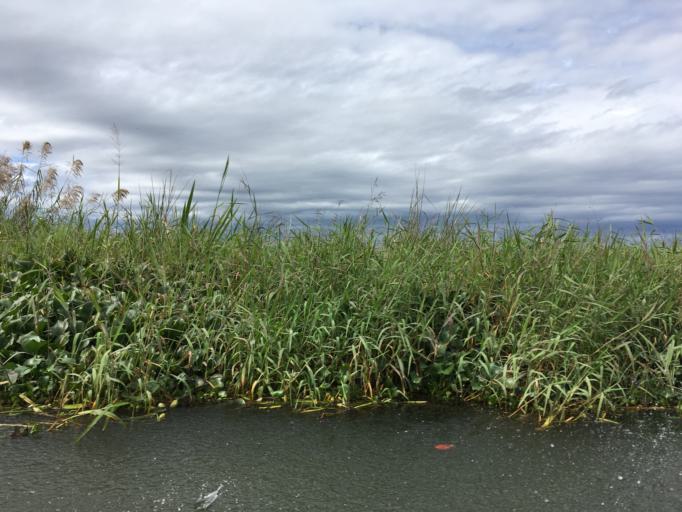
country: MM
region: Shan
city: Taunggyi
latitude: 20.4476
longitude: 96.9036
